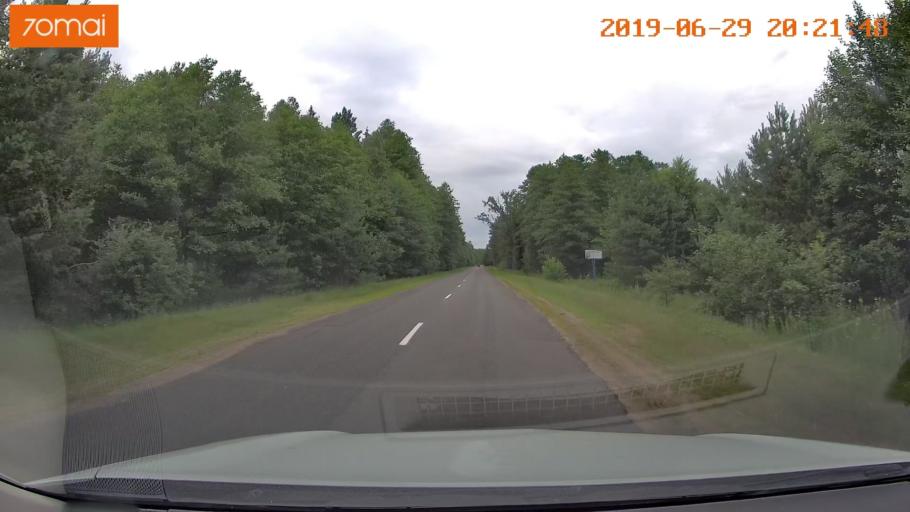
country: BY
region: Brest
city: Asnyezhytsy
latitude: 52.4239
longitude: 26.2533
